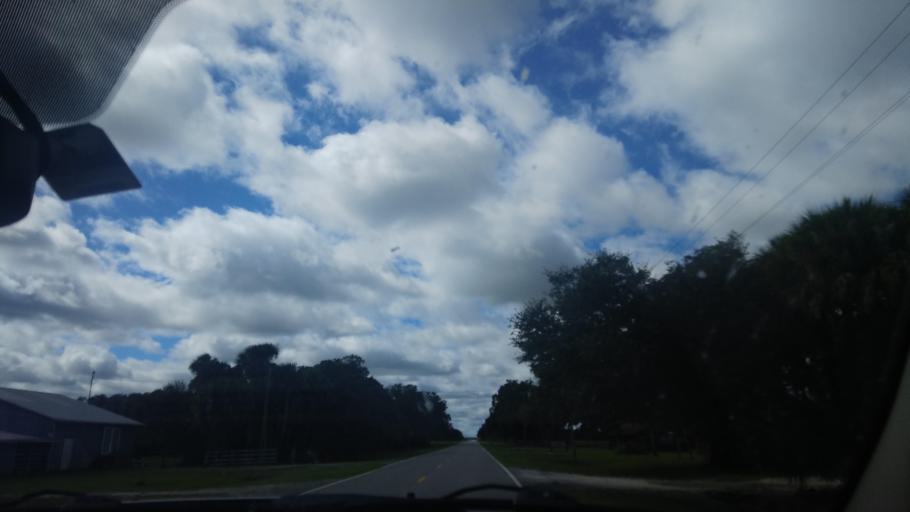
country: US
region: Florida
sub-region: Okeechobee County
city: Okeechobee
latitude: 27.3945
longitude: -80.9163
